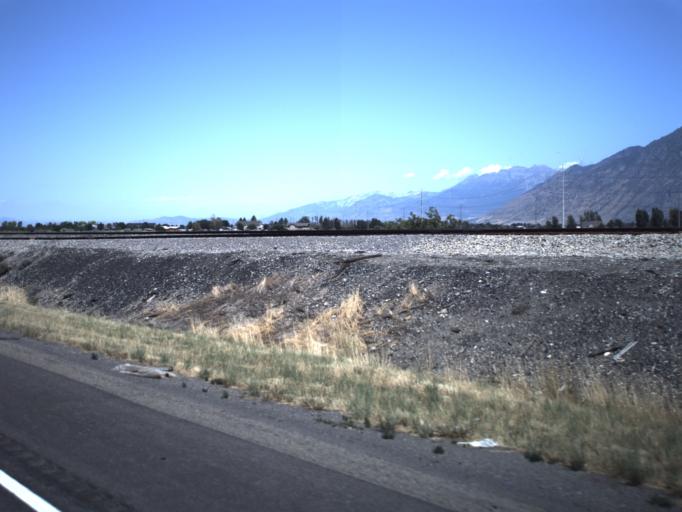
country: US
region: Utah
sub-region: Utah County
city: Mapleton
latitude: 40.0921
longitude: -111.5987
